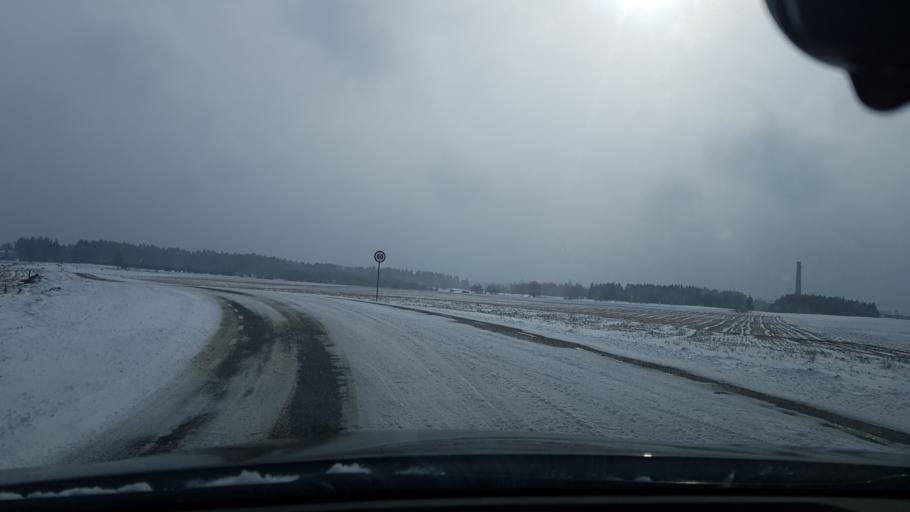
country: EE
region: Harju
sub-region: Kuusalu vald
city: Kuusalu
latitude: 59.4565
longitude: 25.4104
